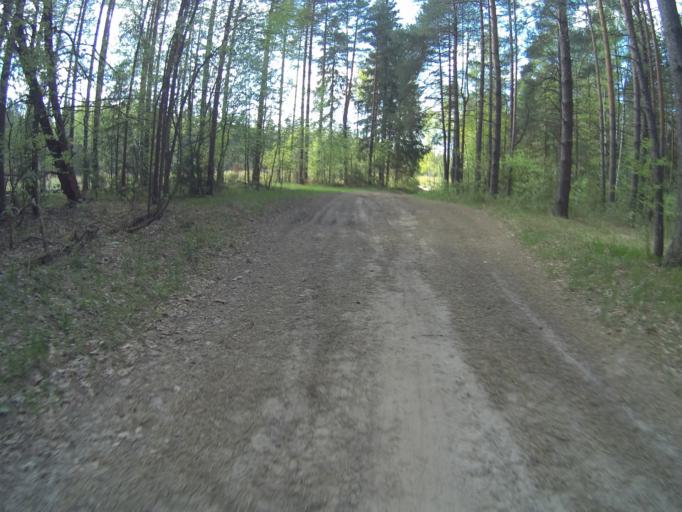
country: RU
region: Vladimir
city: Raduzhnyy
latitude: 56.0146
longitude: 40.2806
